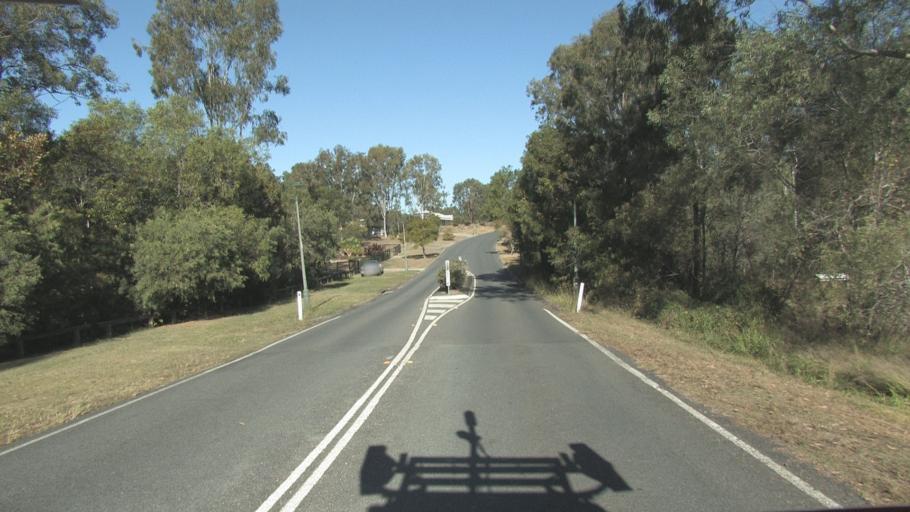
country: AU
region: Queensland
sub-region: Logan
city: Cedar Vale
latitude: -27.8611
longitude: 153.0373
